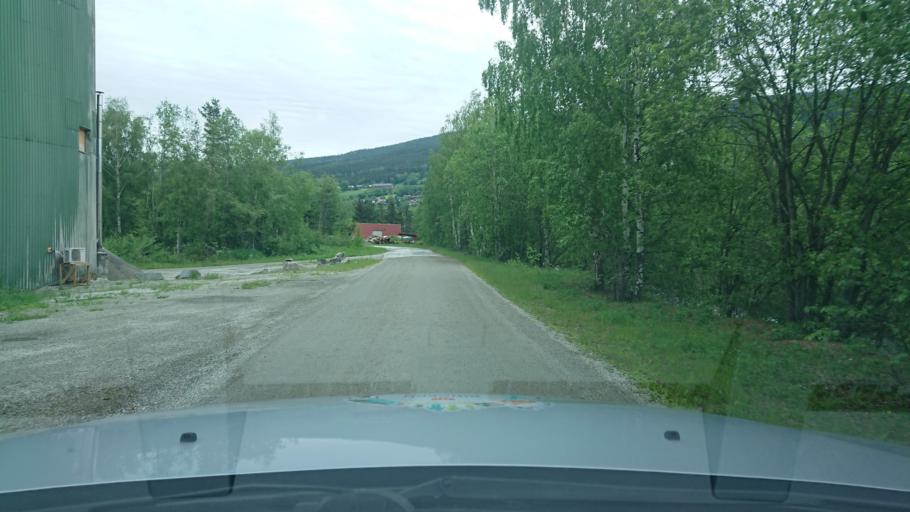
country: NO
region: Oppland
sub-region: Ringebu
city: Ringebu
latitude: 61.5244
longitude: 10.1381
